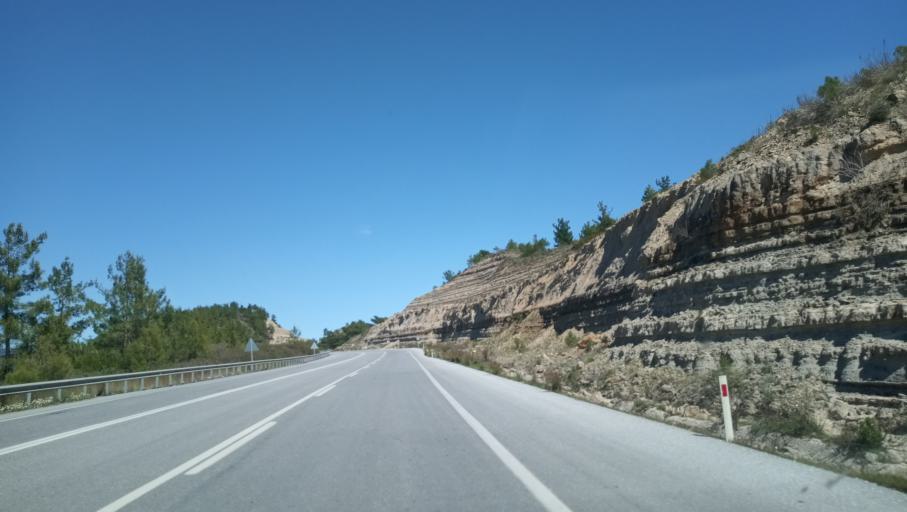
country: TR
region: Antalya
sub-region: Manavgat
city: Kizilagac
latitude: 36.7428
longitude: 31.6163
